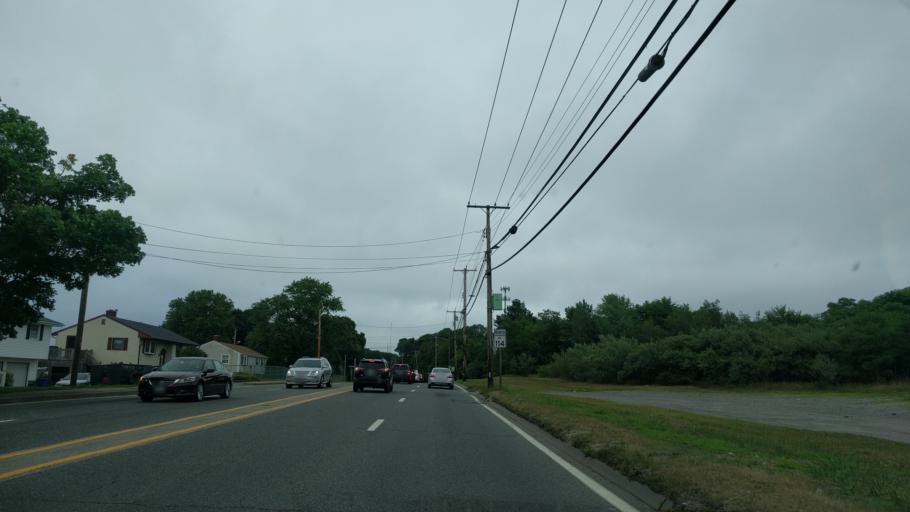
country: US
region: Rhode Island
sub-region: Newport County
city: Middletown
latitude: 41.5594
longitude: -71.2874
